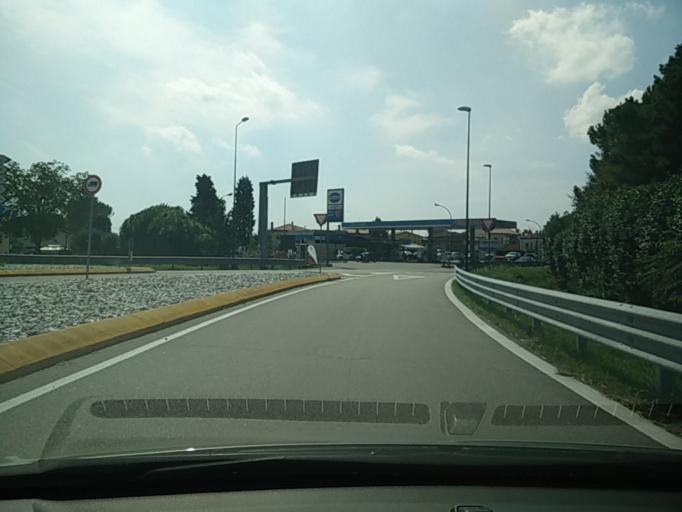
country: IT
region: Veneto
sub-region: Provincia di Treviso
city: Carbonera
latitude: 45.7202
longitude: 12.2851
